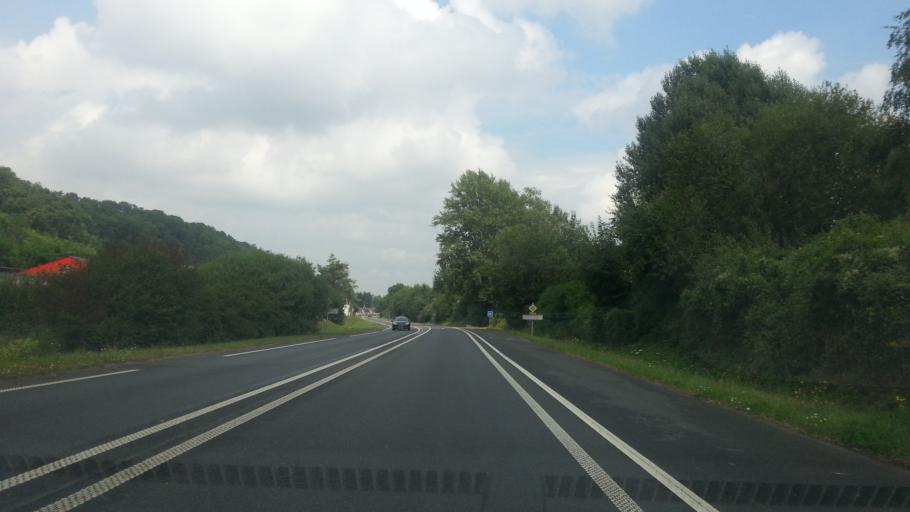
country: FR
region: Picardie
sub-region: Departement de l'Oise
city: Thiverny
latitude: 49.2326
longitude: 2.4350
